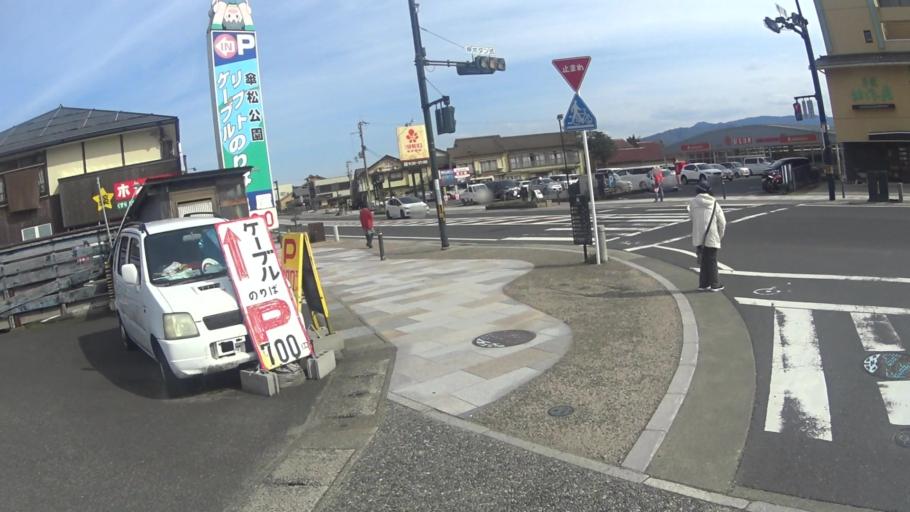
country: JP
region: Kyoto
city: Miyazu
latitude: 35.5815
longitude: 135.1955
